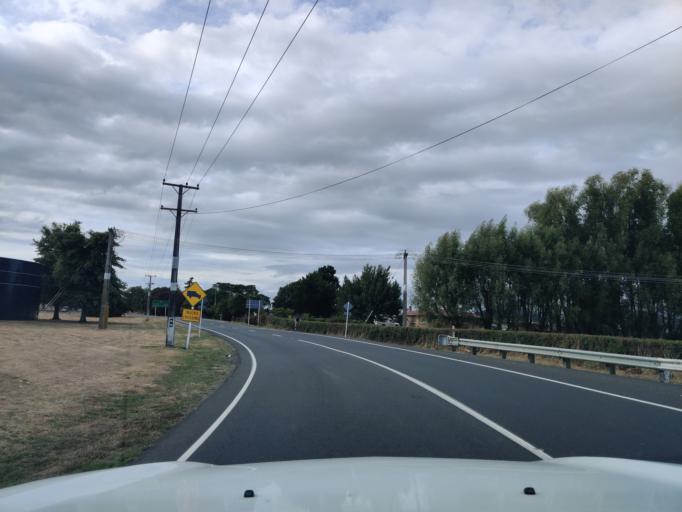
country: NZ
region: Waikato
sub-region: Waipa District
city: Cambridge
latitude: -37.8613
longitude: 175.4552
